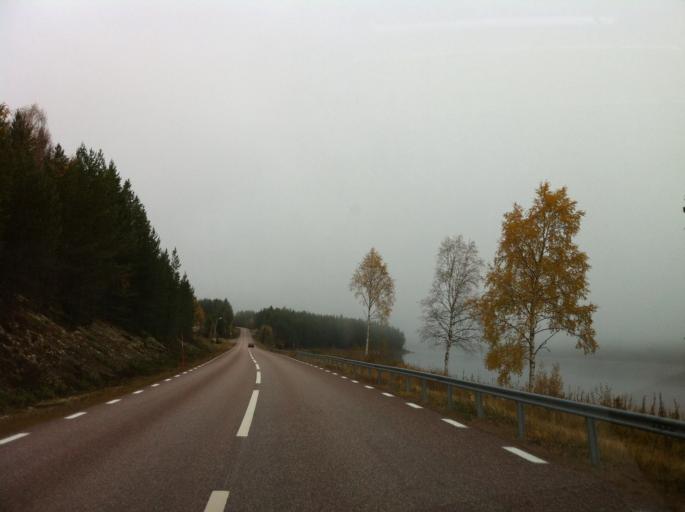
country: NO
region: Hedmark
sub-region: Trysil
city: Innbygda
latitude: 61.7400
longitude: 12.9783
